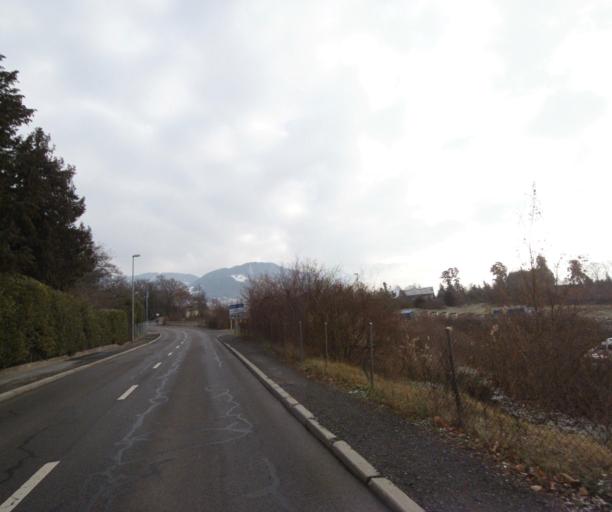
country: CH
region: Vaud
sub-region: Riviera-Pays-d'Enhaut District
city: La Tour-de-Peilz
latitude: 46.4514
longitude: 6.8719
